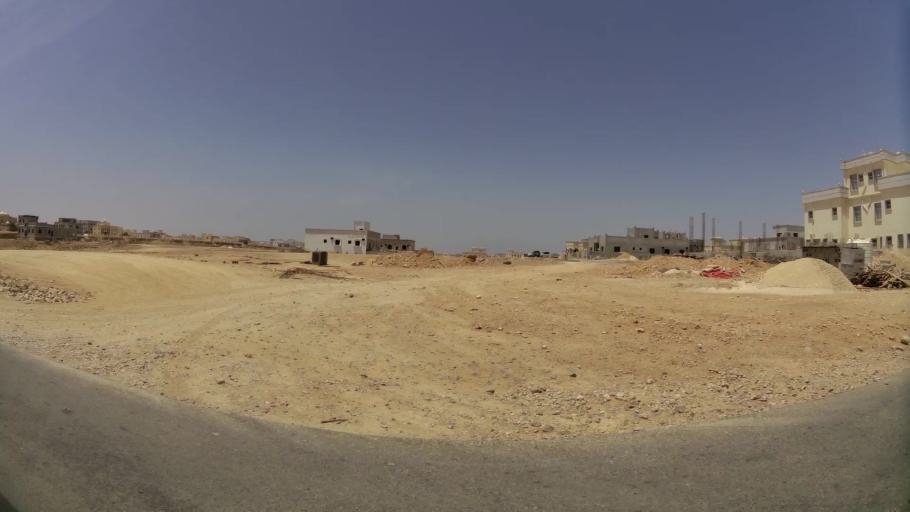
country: OM
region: Zufar
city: Salalah
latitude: 17.0821
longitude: 54.1904
